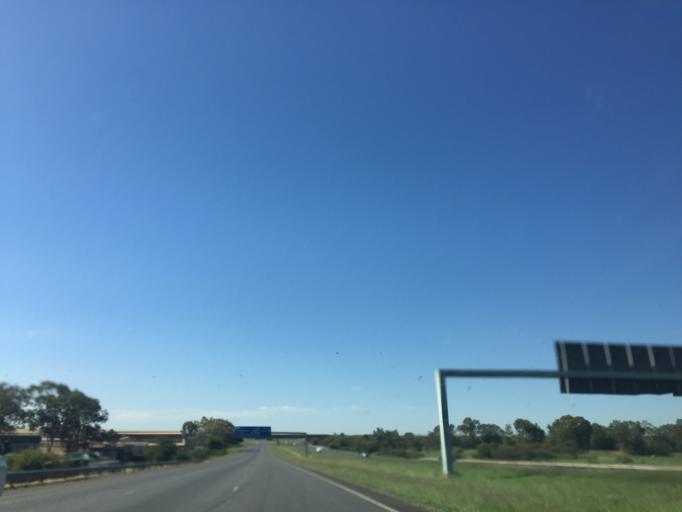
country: ZA
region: Gauteng
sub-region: Sedibeng District Municipality
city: Vereeniging
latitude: -26.6804
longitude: 27.9057
